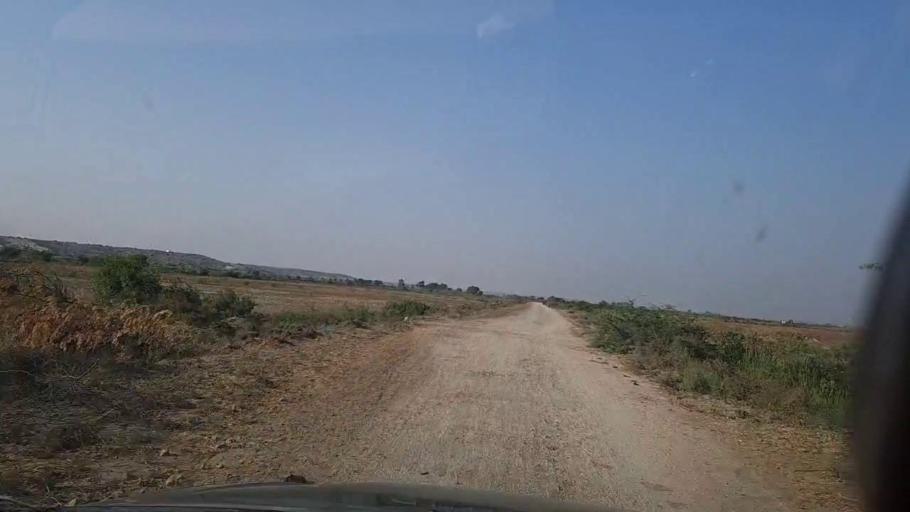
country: PK
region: Sindh
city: Thatta
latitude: 24.5899
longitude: 67.8762
